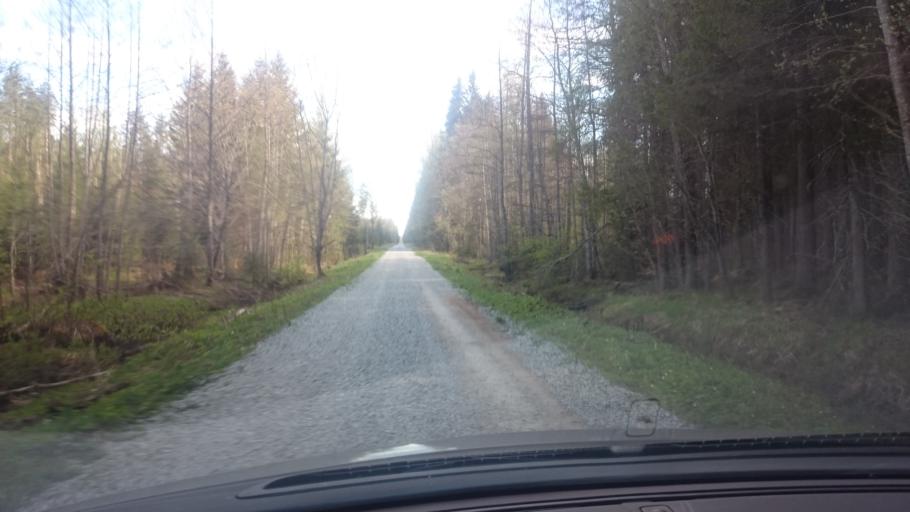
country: EE
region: Ida-Virumaa
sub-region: Sillamaee linn
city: Sillamae
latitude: 59.1693
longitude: 27.7982
